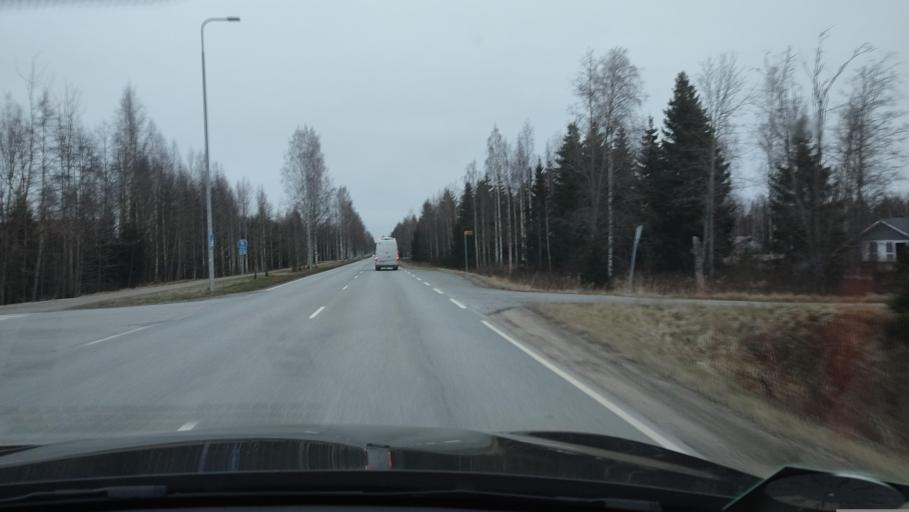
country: FI
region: Southern Ostrobothnia
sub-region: Suupohja
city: Kauhajoki
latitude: 62.4099
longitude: 22.1673
